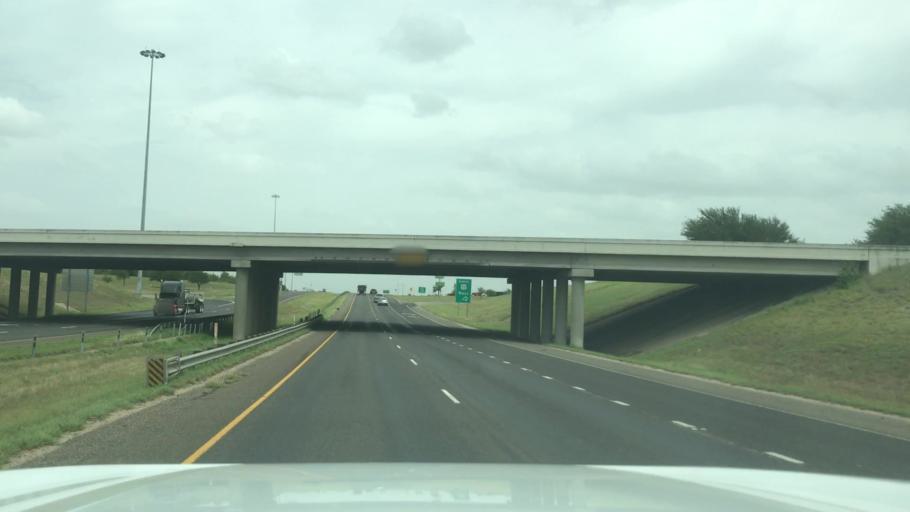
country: US
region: Texas
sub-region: McLennan County
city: Beverly
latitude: 31.4983
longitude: -97.1256
